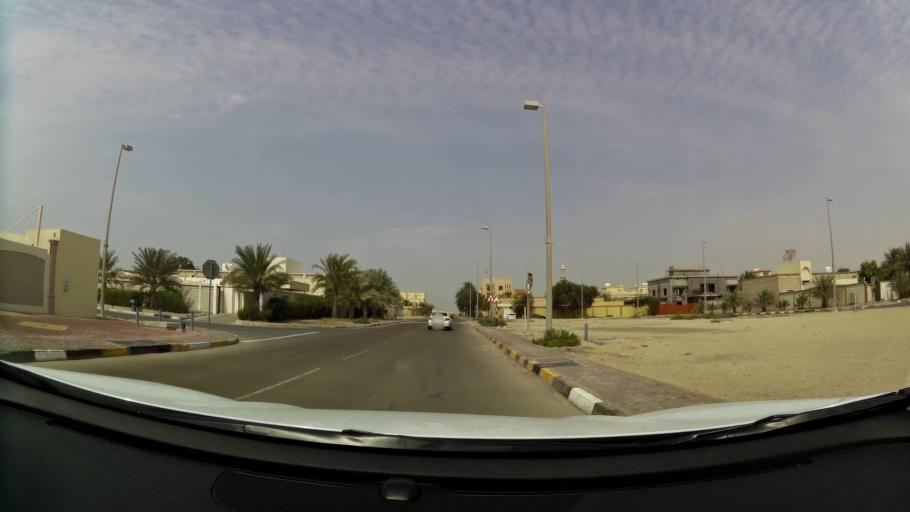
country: AE
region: Abu Dhabi
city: Abu Dhabi
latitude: 24.5306
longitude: 54.6882
